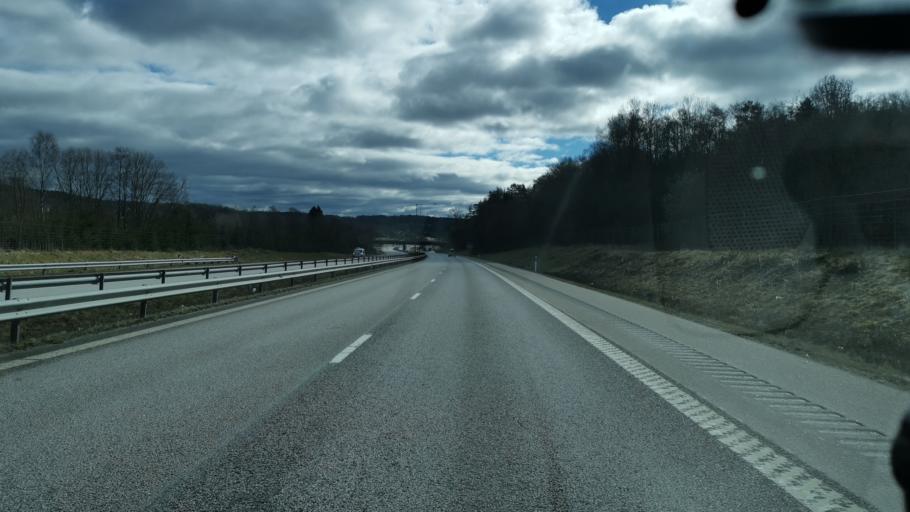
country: SE
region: Vaestra Goetaland
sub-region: Uddevalla Kommun
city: Ljungskile
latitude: 58.2362
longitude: 11.9110
